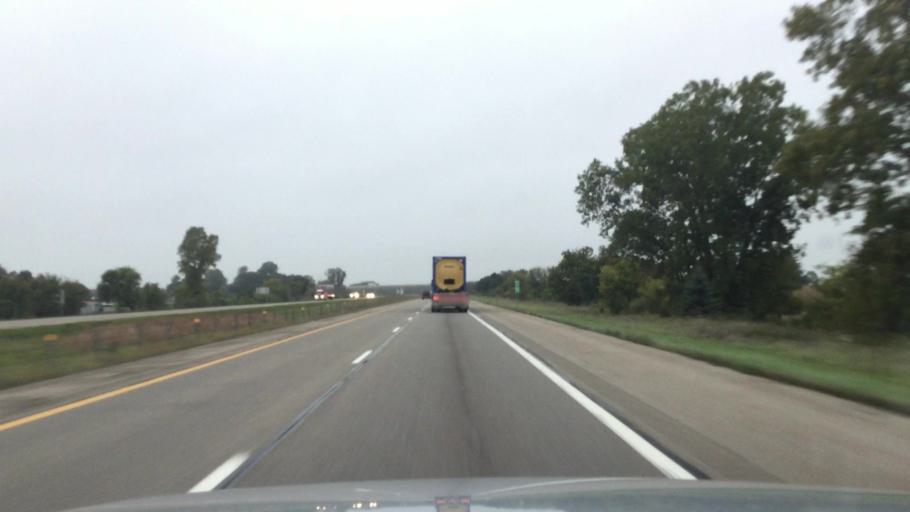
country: US
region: Michigan
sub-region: Shiawassee County
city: Durand
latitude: 42.9220
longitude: -84.0209
